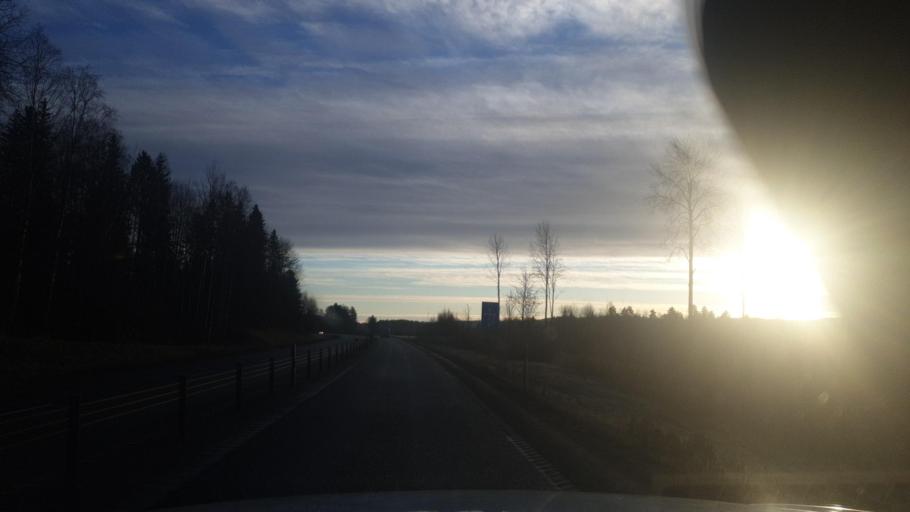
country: SE
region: Vaermland
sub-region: Arvika Kommun
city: Arvika
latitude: 59.6565
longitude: 12.6477
